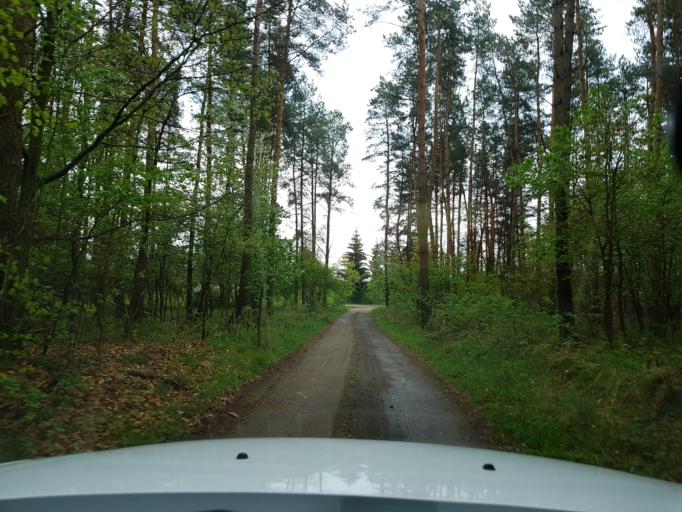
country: PL
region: West Pomeranian Voivodeship
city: Trzcinsko Zdroj
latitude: 52.9905
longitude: 14.6749
